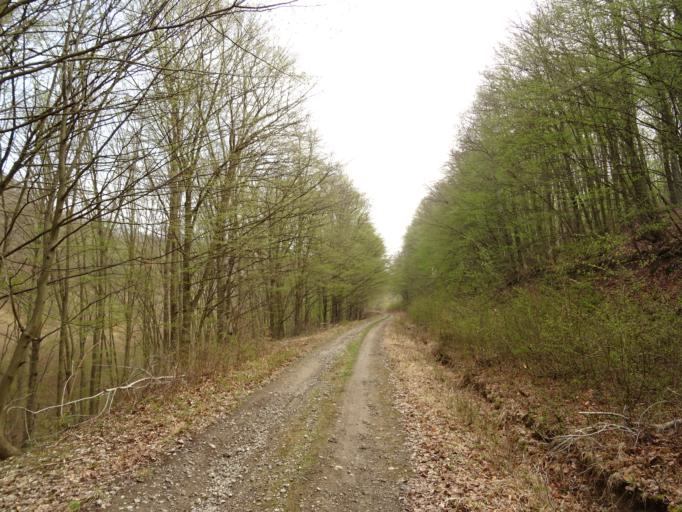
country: HU
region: Nograd
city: Matranovak
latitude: 48.0650
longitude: 20.0243
